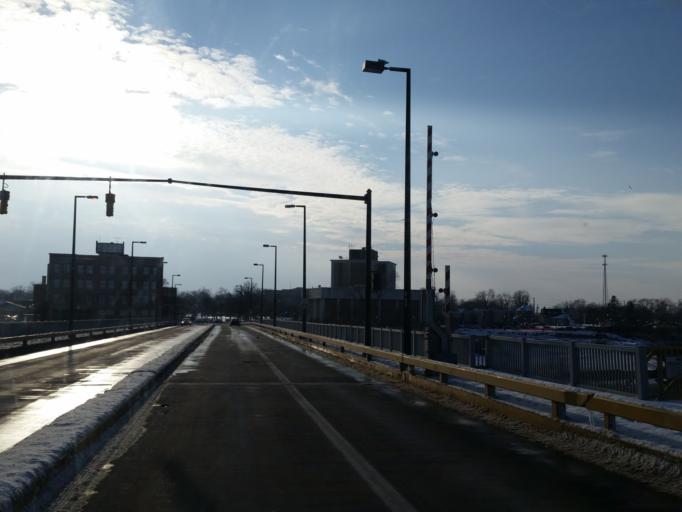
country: US
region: Ohio
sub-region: Lorain County
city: Lorain
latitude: 41.4697
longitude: -82.1759
